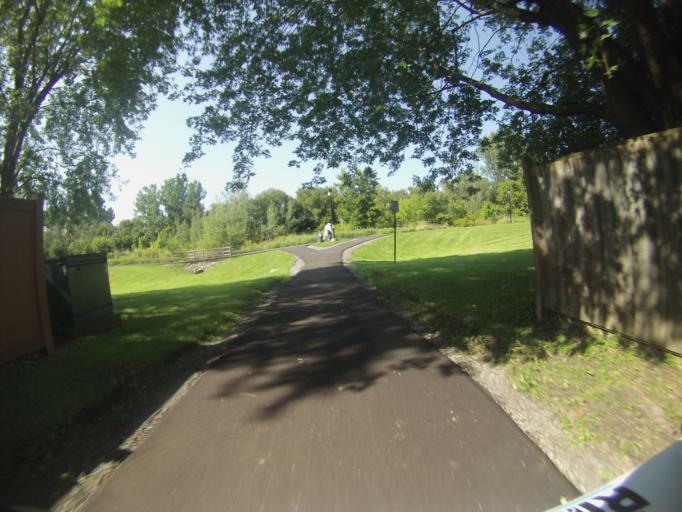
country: CA
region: Ontario
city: Ottawa
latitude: 45.3656
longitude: -75.6410
